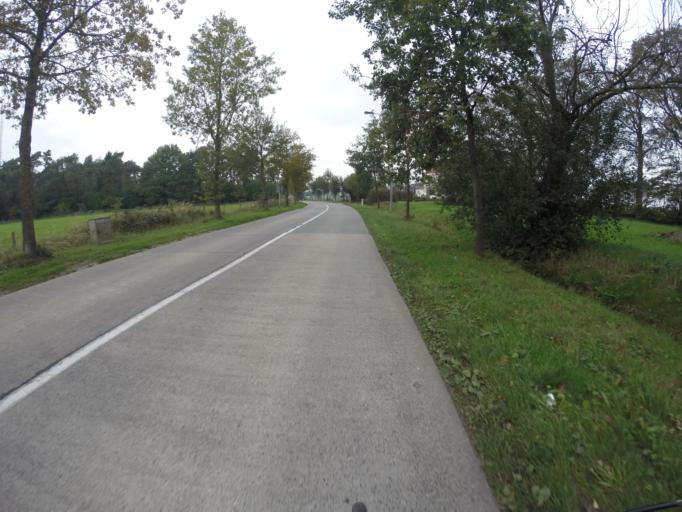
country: BE
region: Flanders
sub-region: Provincie West-Vlaanderen
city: Beernem
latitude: 51.0821
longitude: 3.3490
